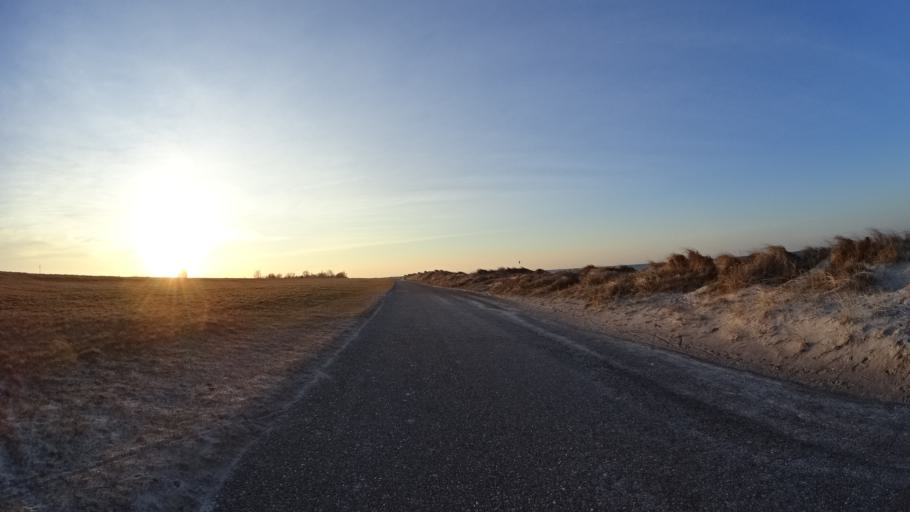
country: DE
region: Schleswig-Holstein
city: Krummbek
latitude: 54.4220
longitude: 10.3991
